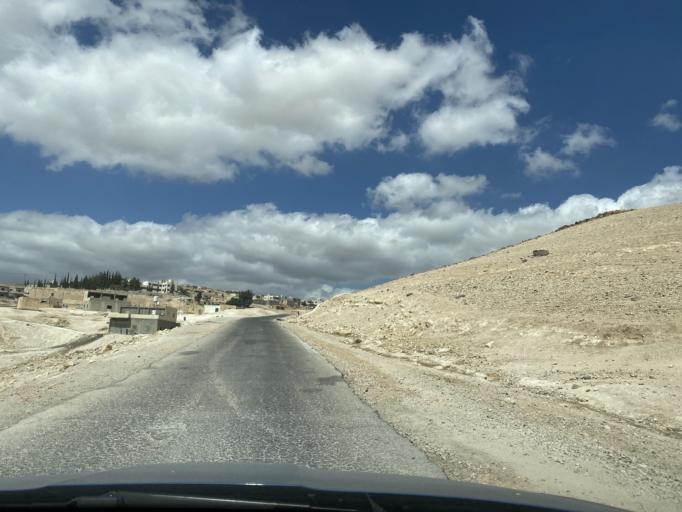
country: PS
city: `Arab ar Rashaydah
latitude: 31.5659
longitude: 35.2395
